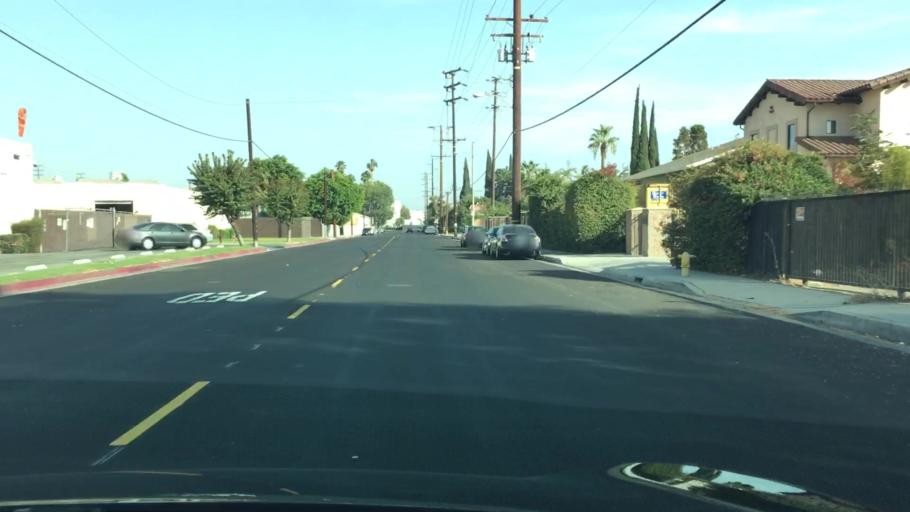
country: US
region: California
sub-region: Los Angeles County
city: Avocado Heights
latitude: 34.0197
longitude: -117.9770
